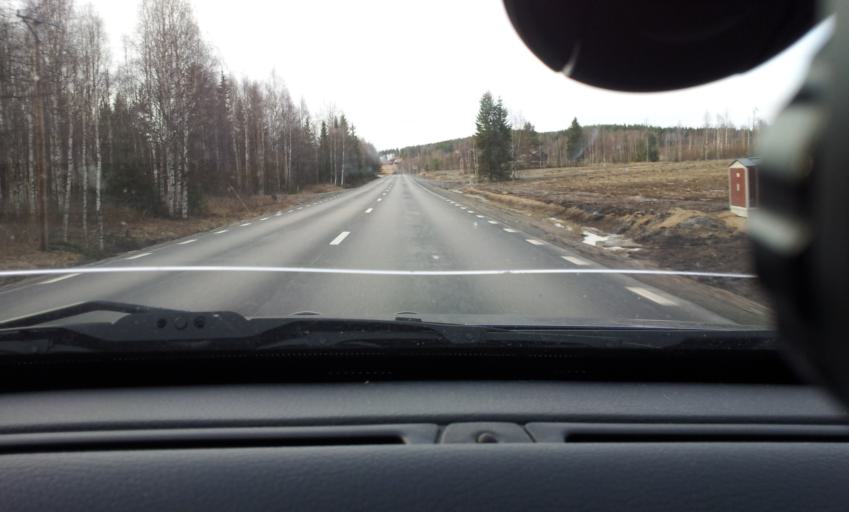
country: SE
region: Gaevleborg
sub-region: Ljusdals Kommun
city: Farila
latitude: 61.8571
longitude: 15.7453
